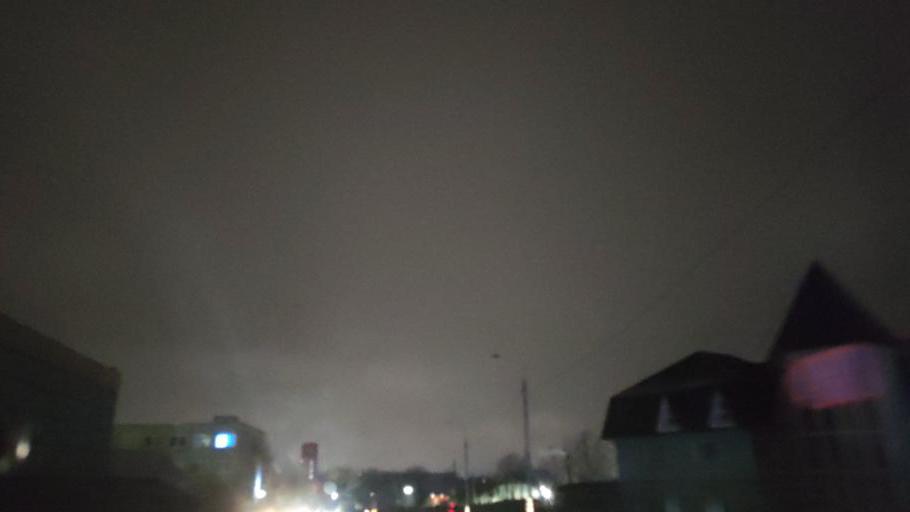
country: RU
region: Moskovskaya
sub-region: Podol'skiy Rayon
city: Podol'sk
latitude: 55.4350
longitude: 37.5926
